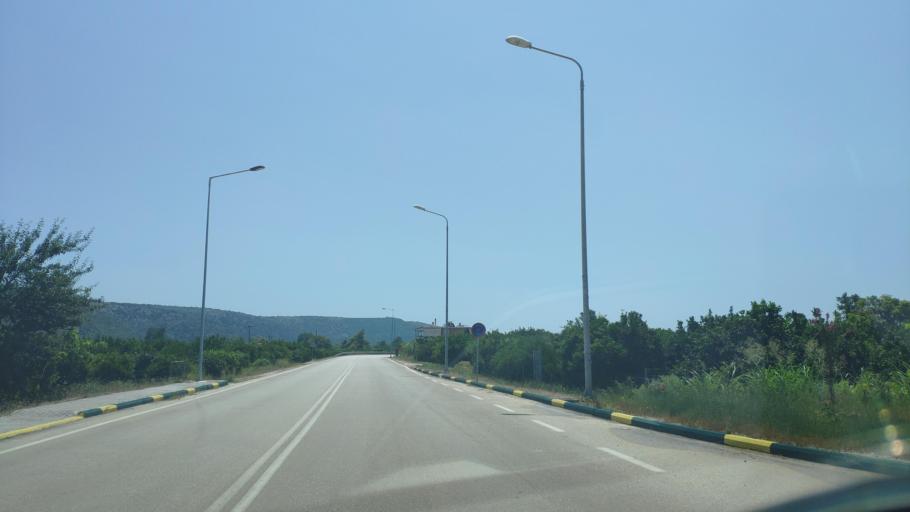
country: GR
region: Epirus
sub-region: Nomos Artas
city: Arta
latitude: 39.1406
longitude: 20.9812
